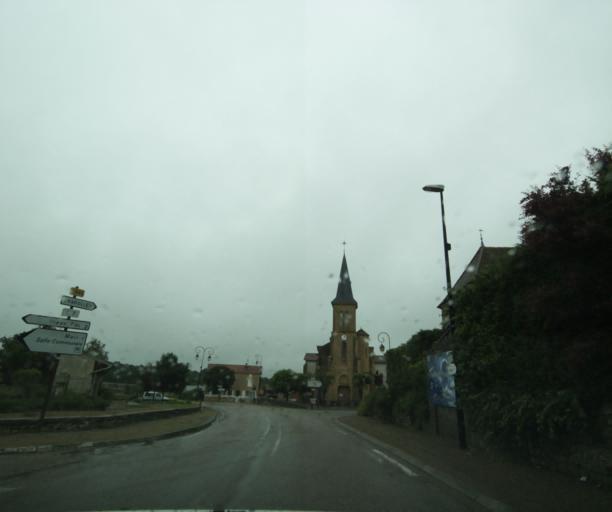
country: FR
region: Bourgogne
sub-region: Departement de Saone-et-Loire
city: Charolles
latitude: 46.4026
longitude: 4.2532
